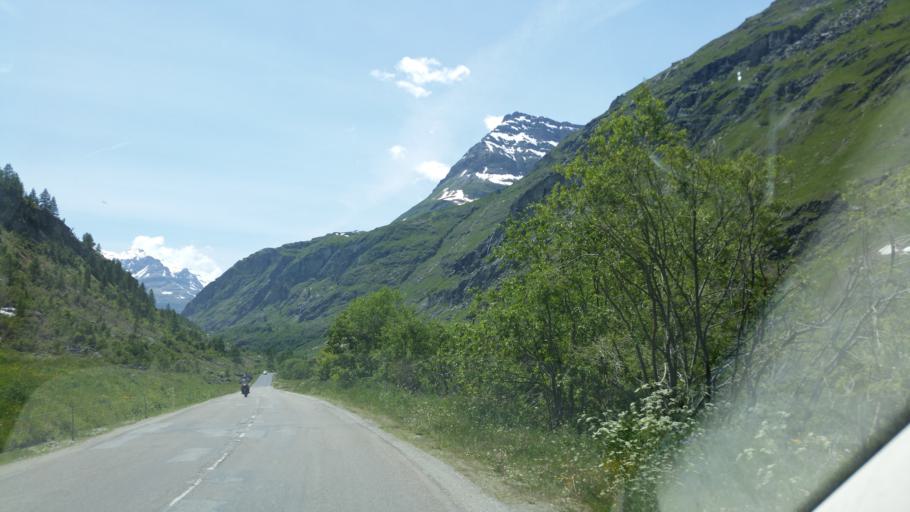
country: FR
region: Rhone-Alpes
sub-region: Departement de la Savoie
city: Val-d'Isere
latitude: 45.3673
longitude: 7.0399
